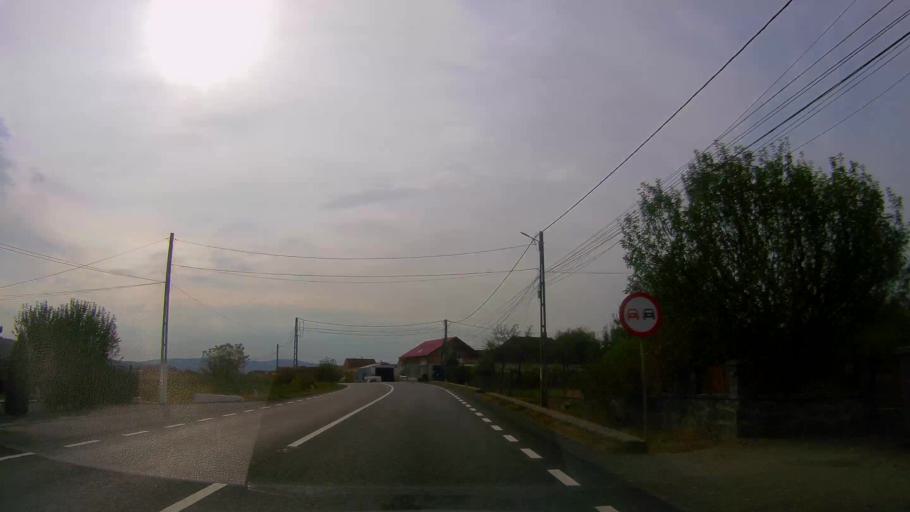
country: RO
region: Salaj
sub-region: Comuna Hereclean
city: Hereclean
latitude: 47.2456
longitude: 22.9869
